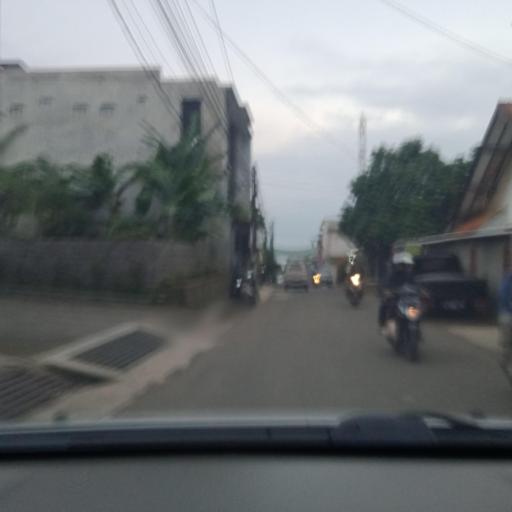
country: ID
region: West Java
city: Cimahi
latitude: -6.8490
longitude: 107.5818
